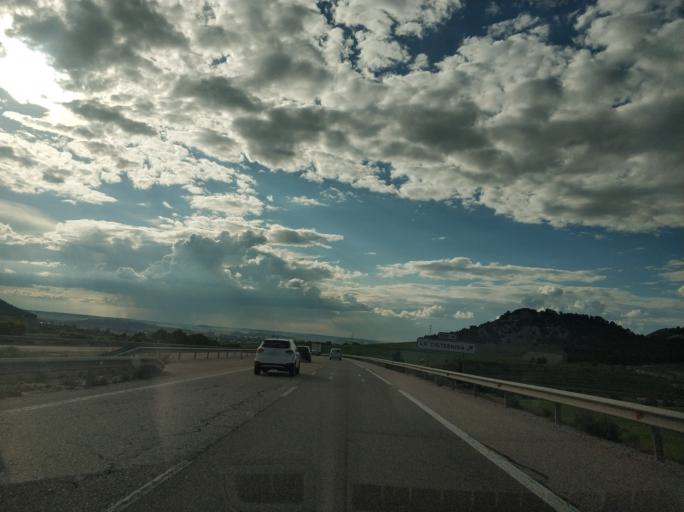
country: ES
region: Castille and Leon
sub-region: Provincia de Valladolid
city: Cisterniga
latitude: 41.6124
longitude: -4.6722
